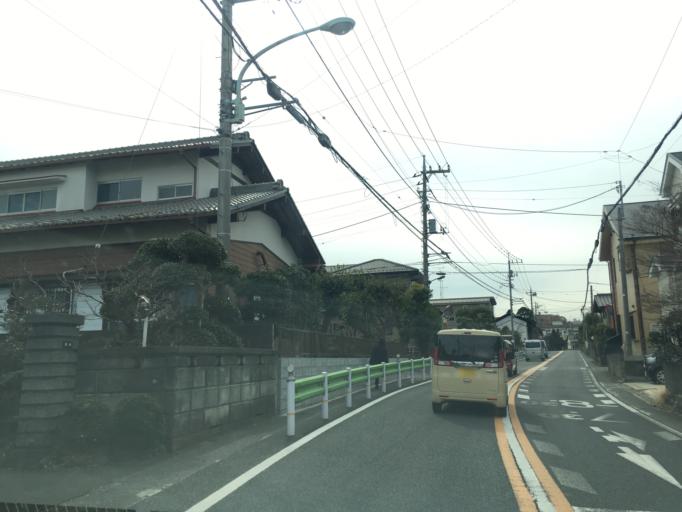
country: JP
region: Tokyo
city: Hino
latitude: 35.6464
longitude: 139.4384
